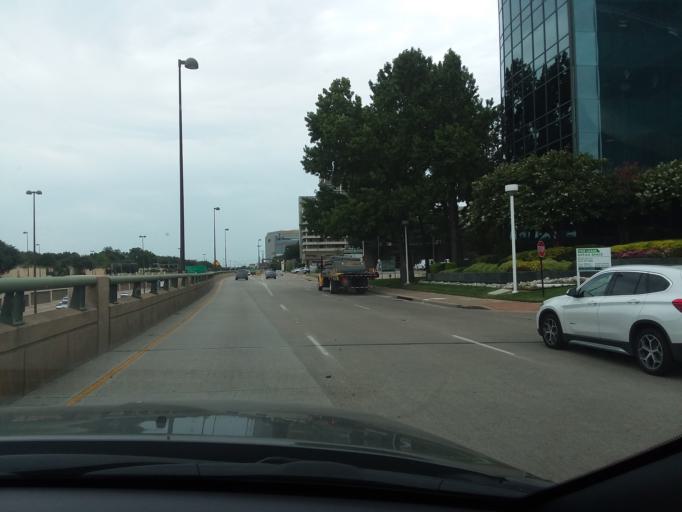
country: US
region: Texas
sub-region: Dallas County
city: Highland Park
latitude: 32.8389
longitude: -96.7768
